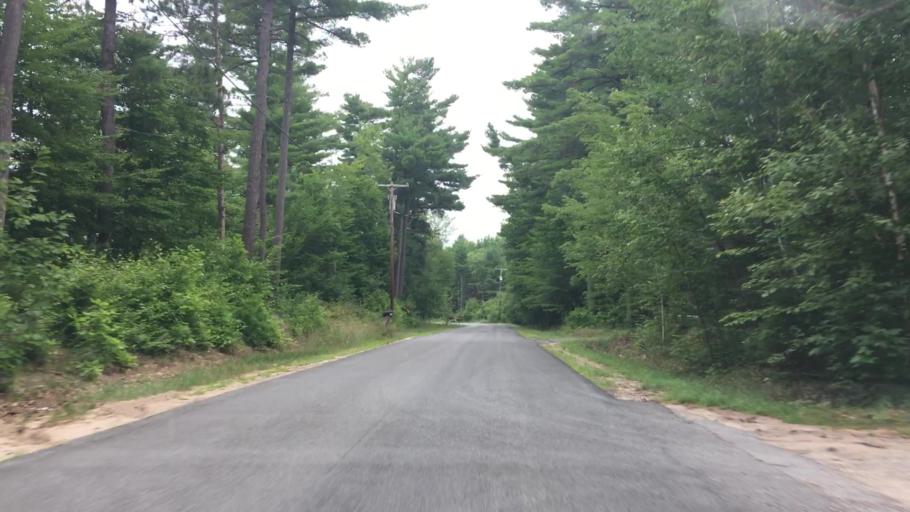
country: US
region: New York
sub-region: Clinton County
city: Peru
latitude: 44.6031
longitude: -73.5932
